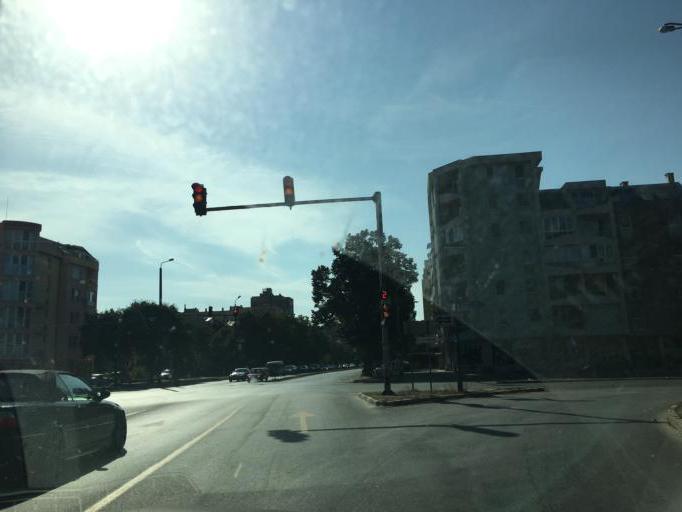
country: BG
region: Pazardzhik
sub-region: Obshtina Pazardzhik
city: Pazardzhik
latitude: 42.2070
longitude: 24.3283
